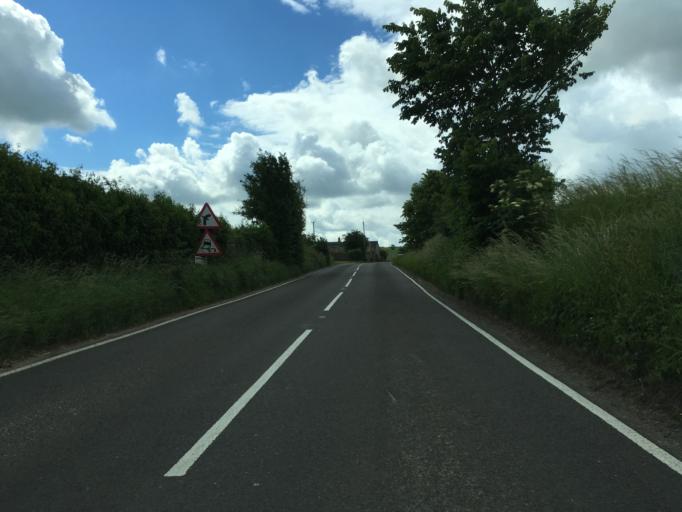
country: GB
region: England
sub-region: Oxfordshire
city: Shipton under Wychwood
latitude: 51.8513
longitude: -1.6013
